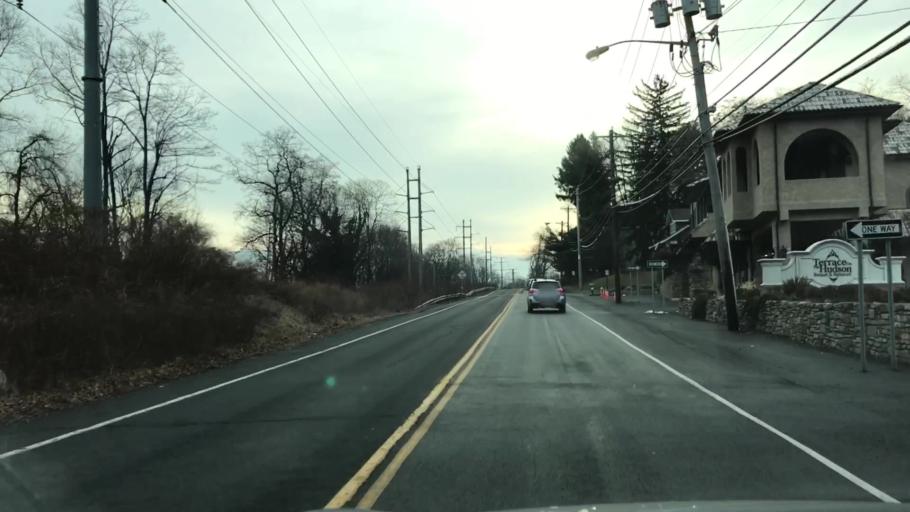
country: US
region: New York
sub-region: Rockland County
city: Haverstraw
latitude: 41.1930
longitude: -73.9667
